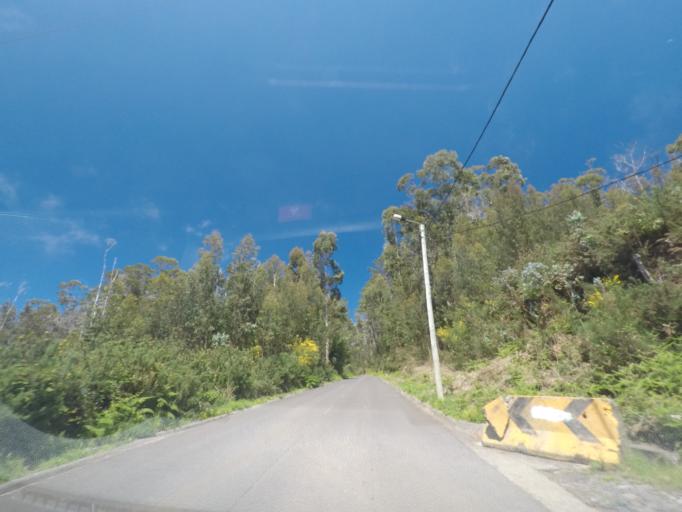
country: PT
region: Madeira
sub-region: Calheta
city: Arco da Calheta
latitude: 32.7331
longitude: -17.1309
